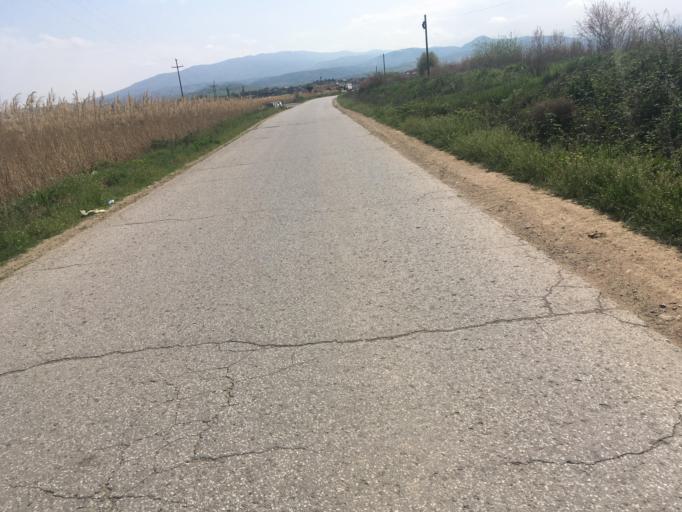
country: MK
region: Karbinci
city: Karbinci
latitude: 41.8009
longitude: 22.2125
